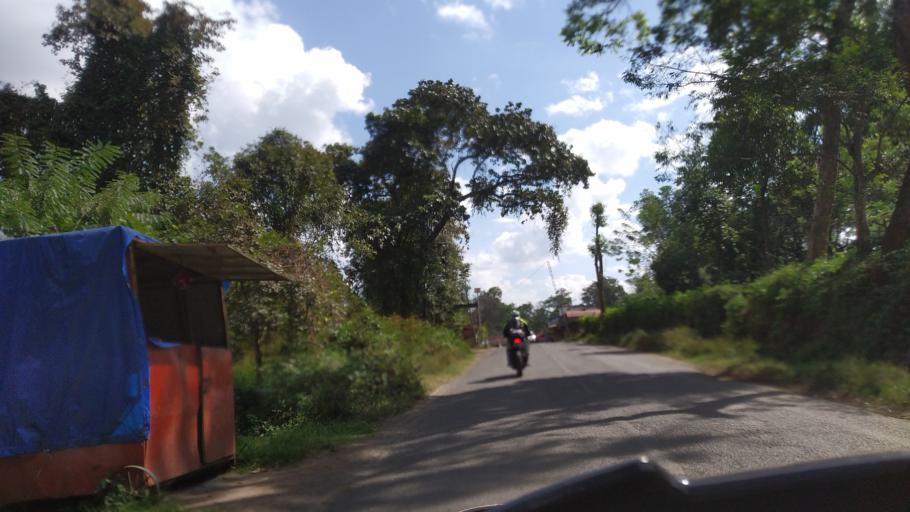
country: IN
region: Karnataka
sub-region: Kodagu
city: Ponnampet
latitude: 11.9586
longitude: 76.0625
